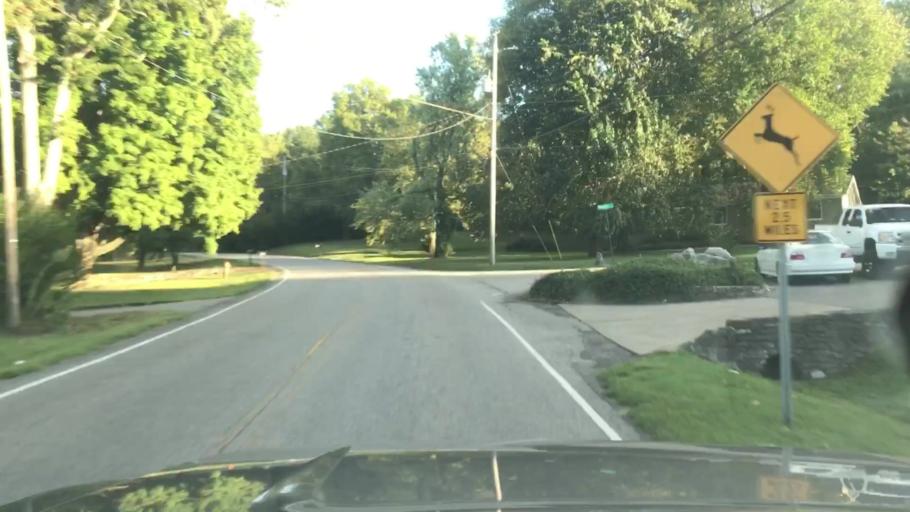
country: US
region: Tennessee
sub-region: Davidson County
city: Belle Meade
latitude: 36.1380
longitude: -86.8796
